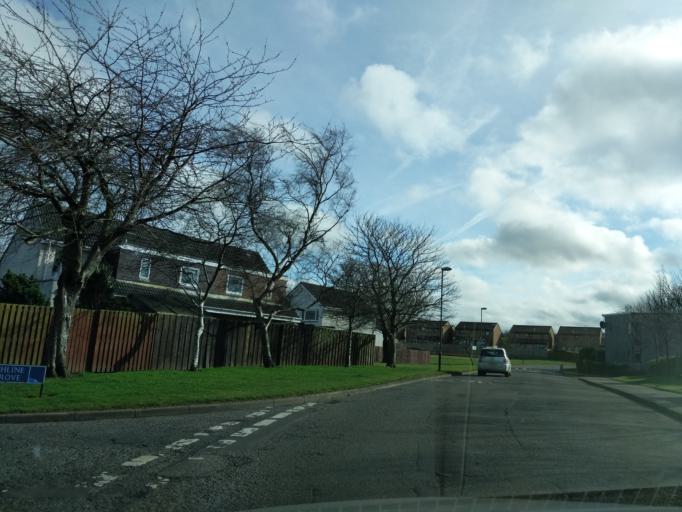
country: GB
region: Scotland
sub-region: Edinburgh
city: Queensferry
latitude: 55.9887
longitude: -3.4086
